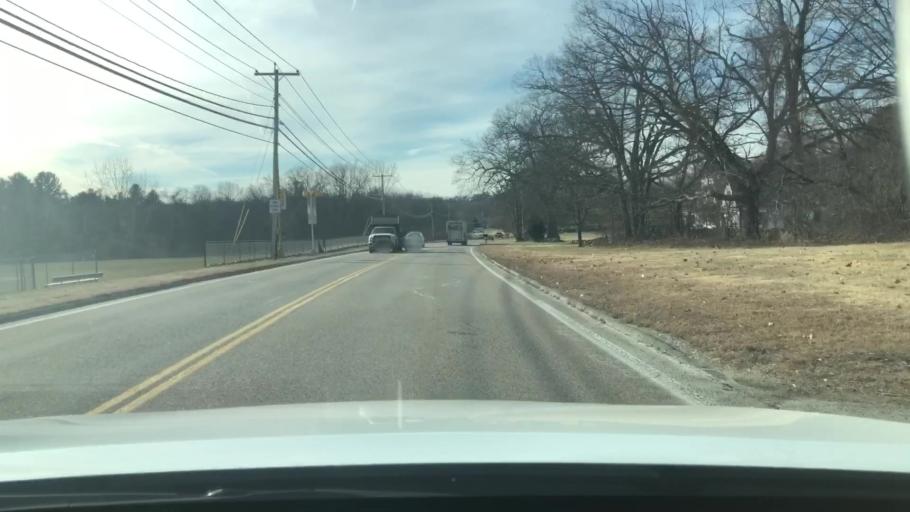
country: US
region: Massachusetts
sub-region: Worcester County
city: Grafton
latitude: 42.1989
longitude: -71.7119
